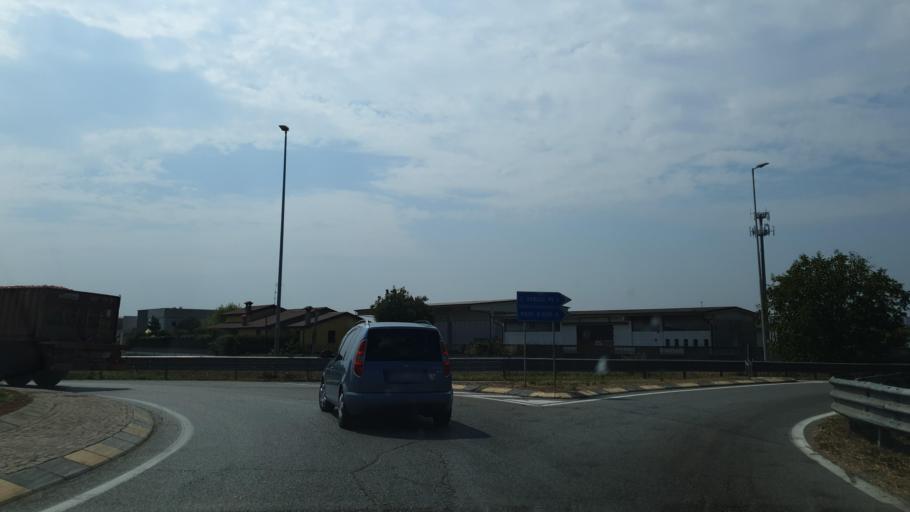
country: IT
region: Lombardy
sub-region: Provincia di Cremona
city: San Daniele Po
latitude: 45.0620
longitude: 10.1908
